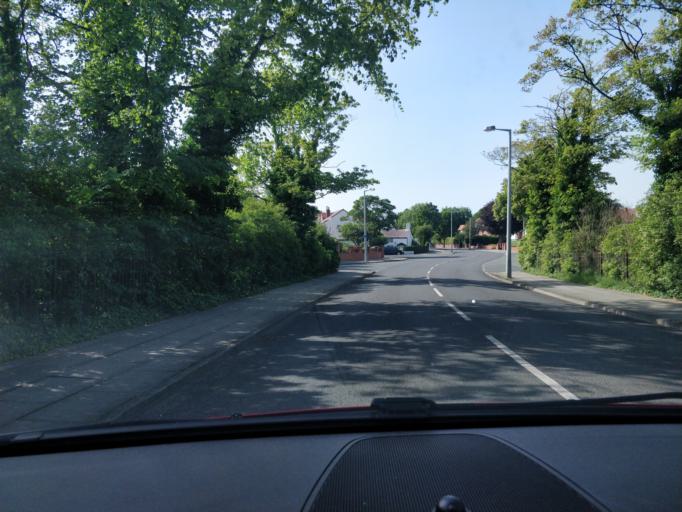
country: GB
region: England
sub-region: Sefton
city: Southport
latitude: 53.6579
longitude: -2.9771
